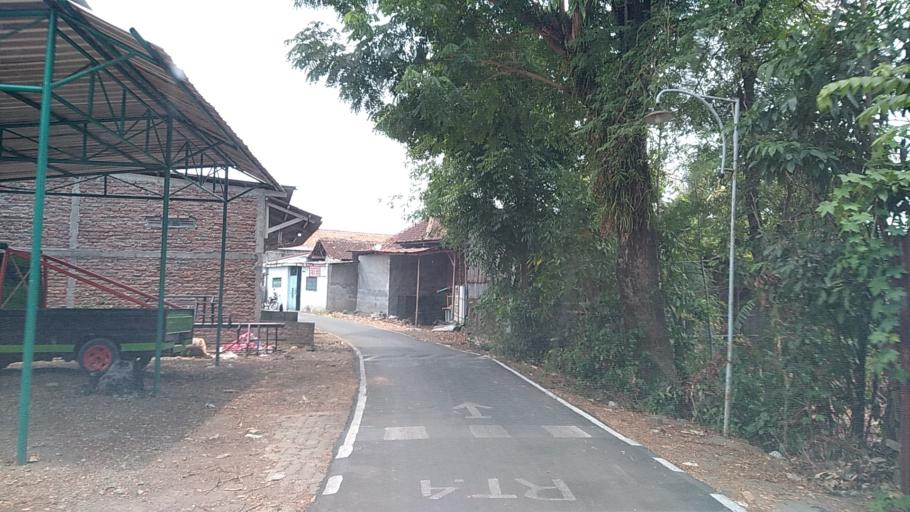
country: ID
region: Central Java
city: Mranggen
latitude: -7.0167
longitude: 110.4703
